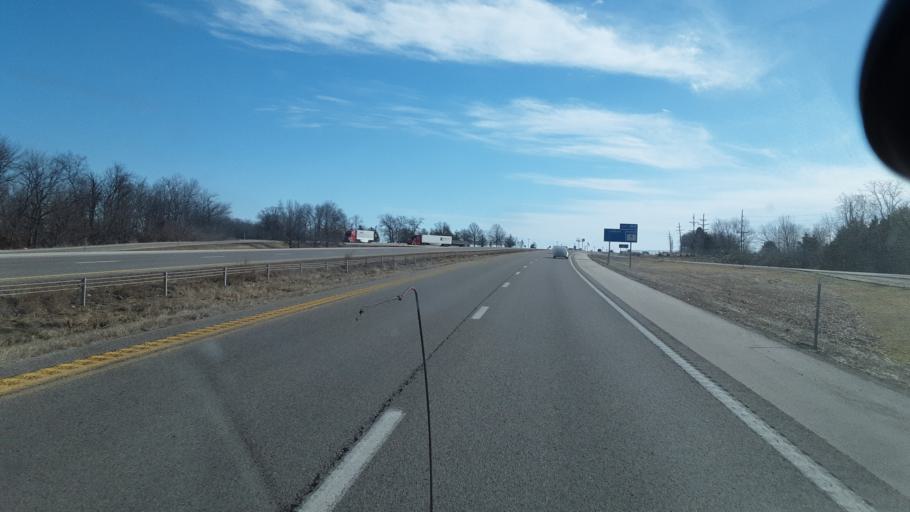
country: US
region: Missouri
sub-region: Warren County
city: Wright City
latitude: 38.8276
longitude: -91.0541
